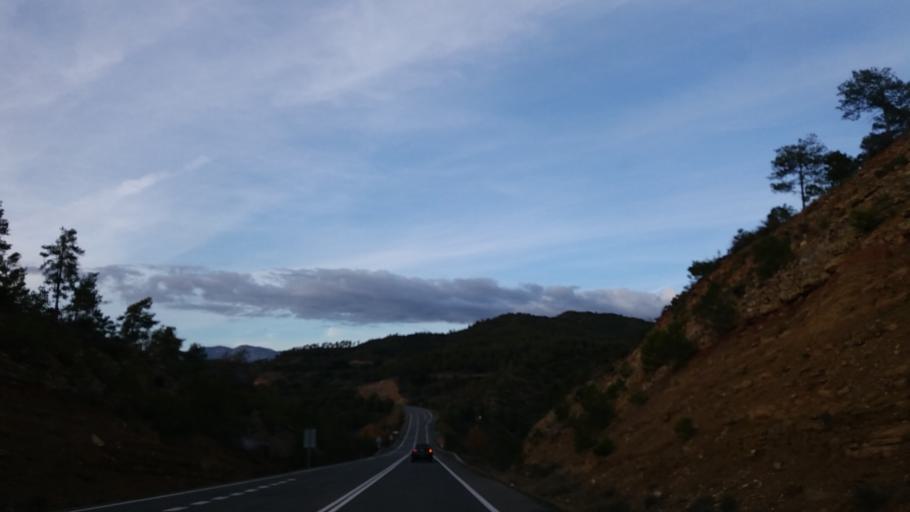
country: ES
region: Catalonia
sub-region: Provincia de Lleida
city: Tiurana
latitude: 41.9706
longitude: 1.2973
